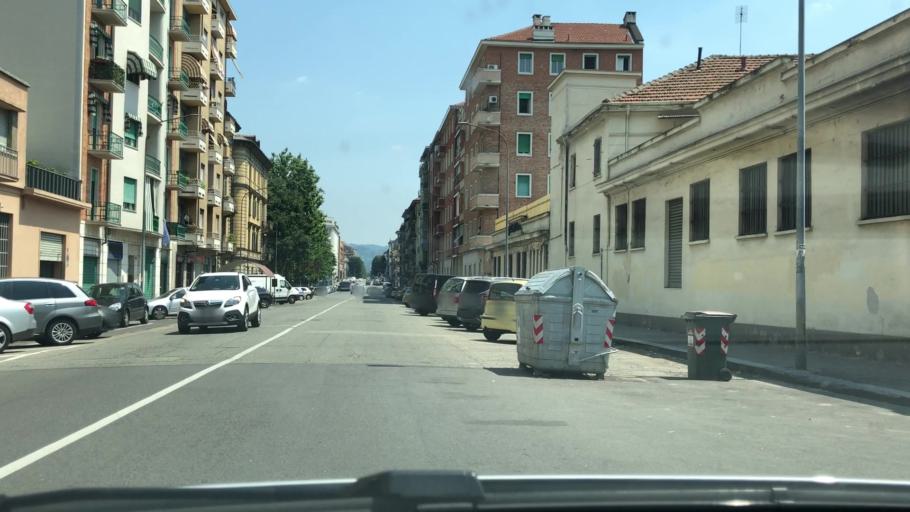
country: IT
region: Piedmont
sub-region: Provincia di Torino
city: Turin
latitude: 45.0848
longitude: 7.6819
